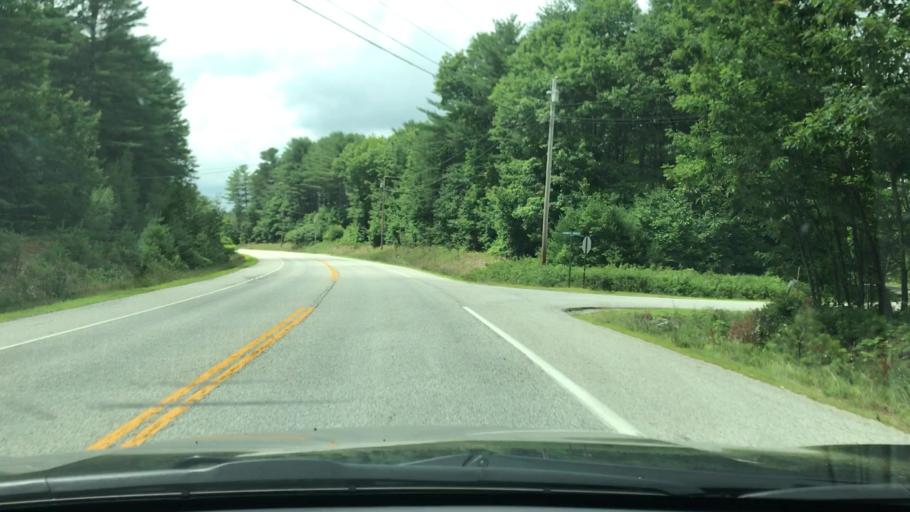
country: US
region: Maine
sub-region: Oxford County
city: Bethel
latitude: 44.3989
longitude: -70.6844
